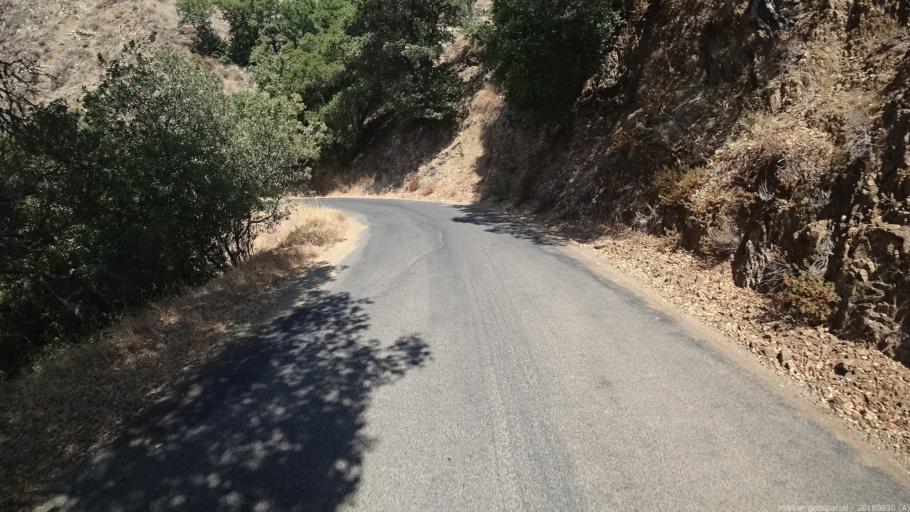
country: US
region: California
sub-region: Monterey County
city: Greenfield
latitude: 35.9984
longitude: -121.4635
